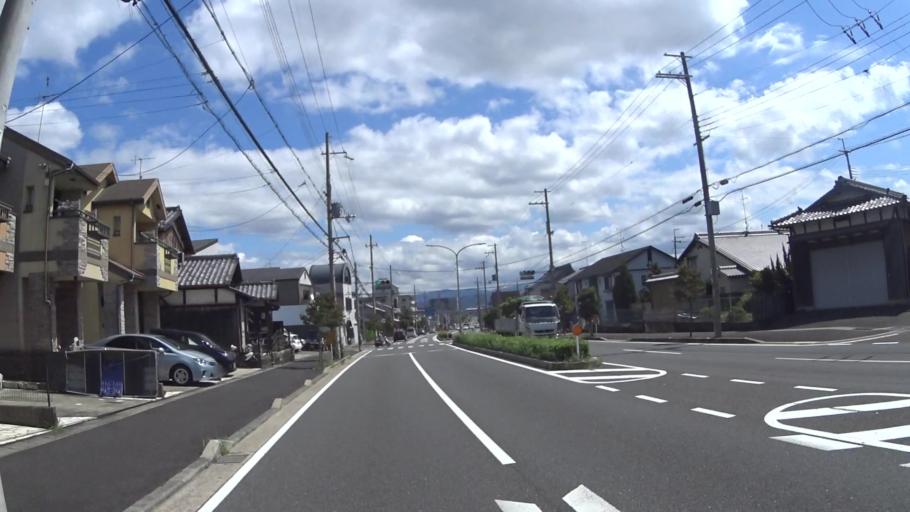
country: JP
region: Kyoto
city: Muko
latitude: 34.9640
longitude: 135.6932
